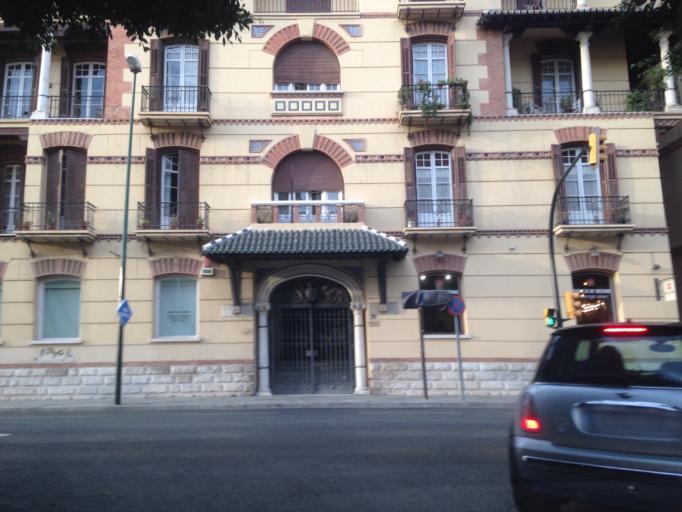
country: ES
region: Andalusia
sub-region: Provincia de Malaga
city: Malaga
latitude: 36.7208
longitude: -4.4090
